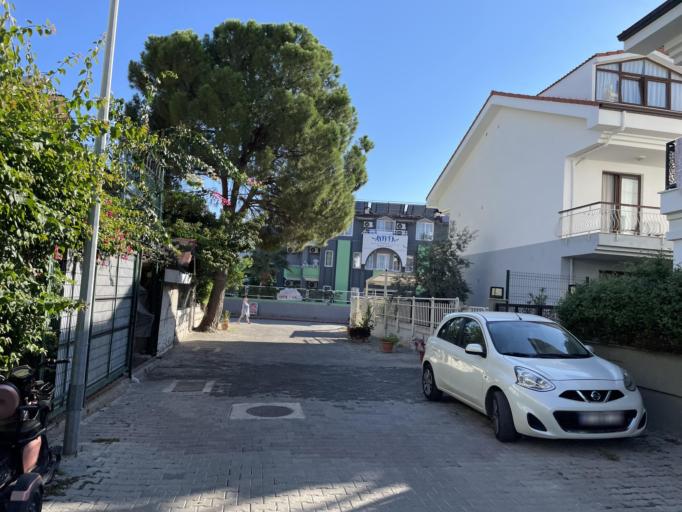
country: TR
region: Antalya
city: Kemer
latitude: 36.6008
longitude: 30.5644
